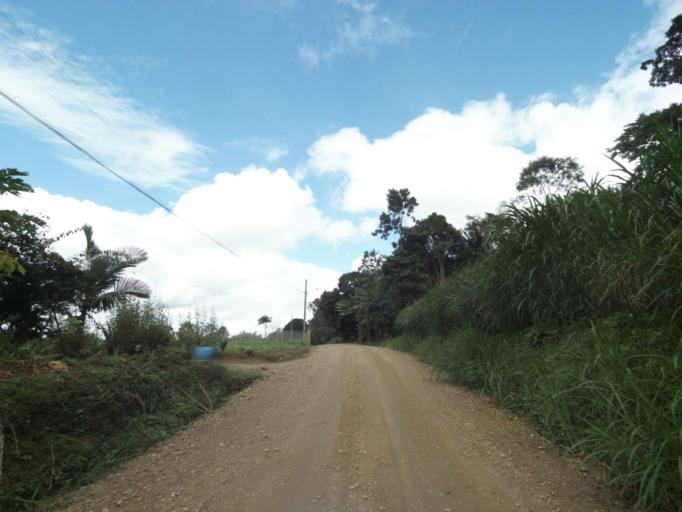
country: BR
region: Santa Catarina
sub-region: Pomerode
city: Pomerode
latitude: -26.6723
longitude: -49.1889
